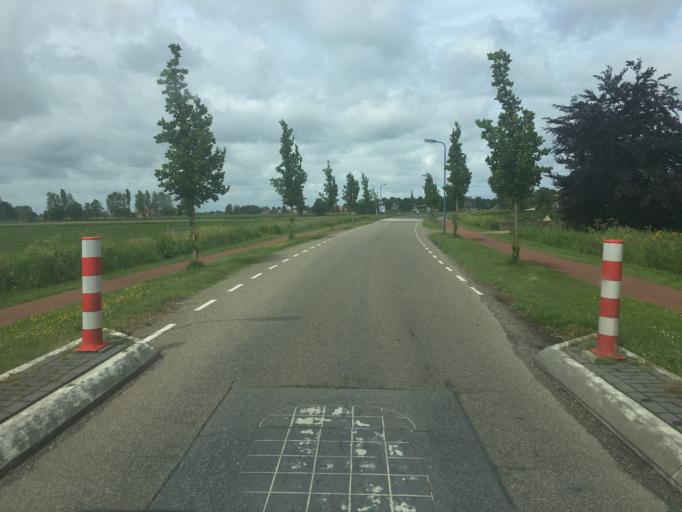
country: NL
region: Friesland
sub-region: Gemeente Lemsterland
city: Echtenerbrug
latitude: 52.8722
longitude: 5.8140
